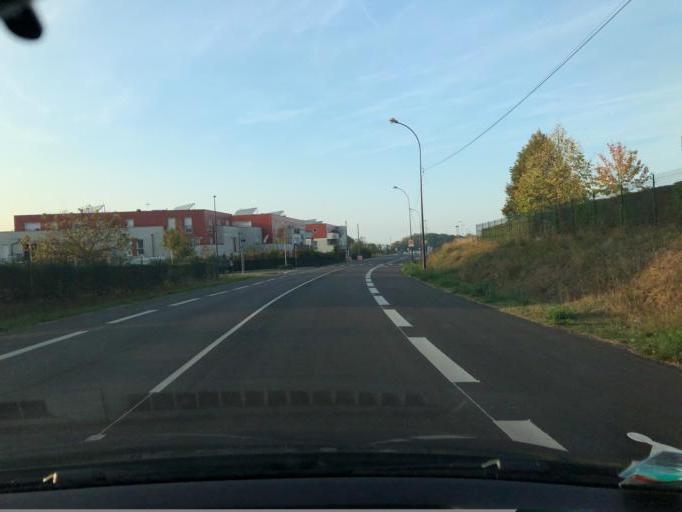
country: FR
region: Bourgogne
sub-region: Departement de l'Yonne
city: Saint-Clement
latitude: 48.2053
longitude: 3.2943
